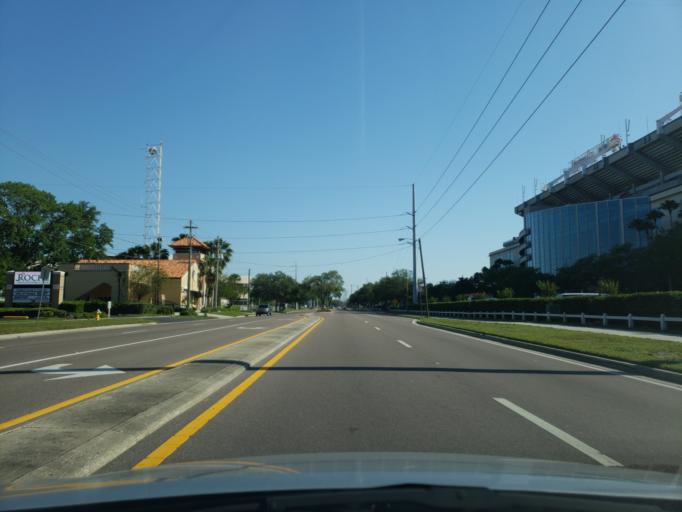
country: US
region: Florida
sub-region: Hillsborough County
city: Egypt Lake-Leto
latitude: 27.9773
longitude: -82.5014
